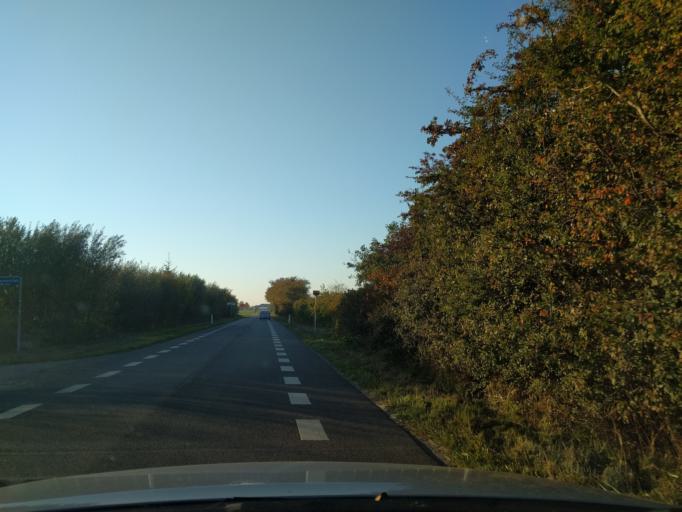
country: DK
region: Zealand
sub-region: Guldborgsund Kommune
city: Nykobing Falster
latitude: 54.7138
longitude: 11.9760
